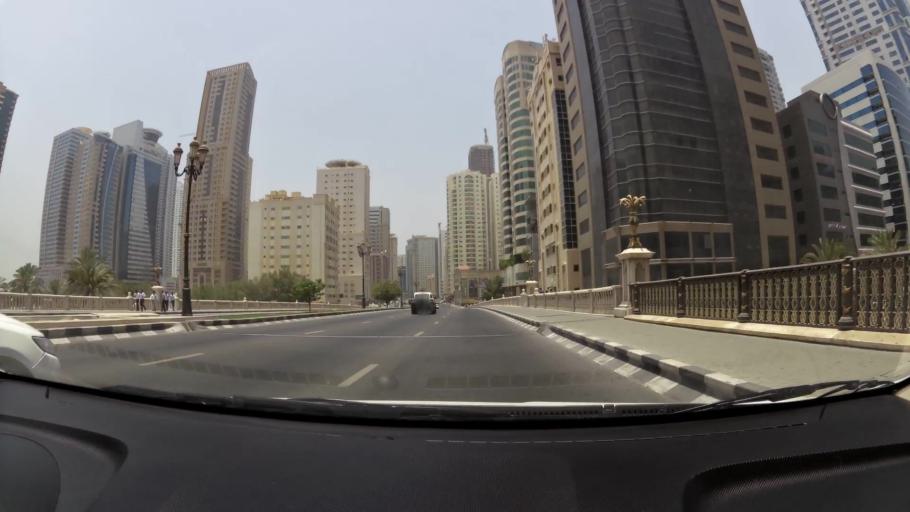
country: AE
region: Ash Shariqah
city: Sharjah
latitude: 25.3232
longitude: 55.3785
